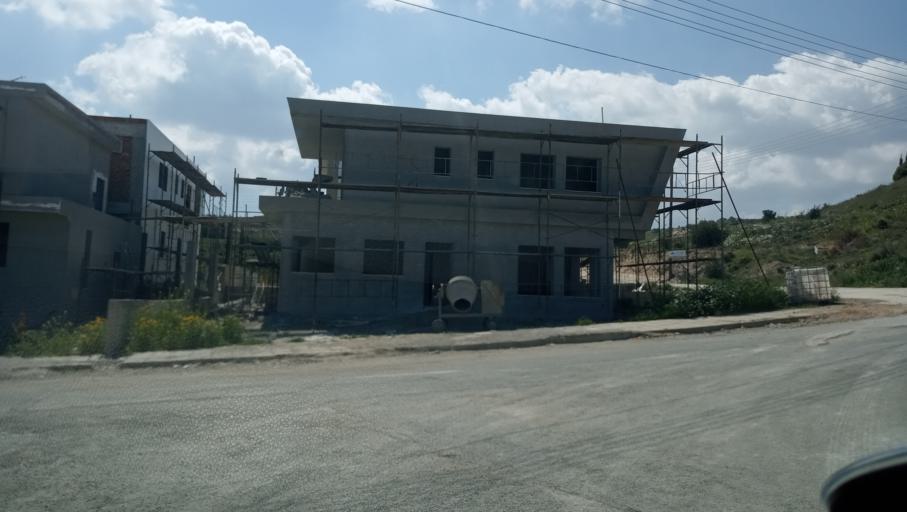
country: CY
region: Lefkosia
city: Alampra
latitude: 35.0101
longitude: 33.4018
